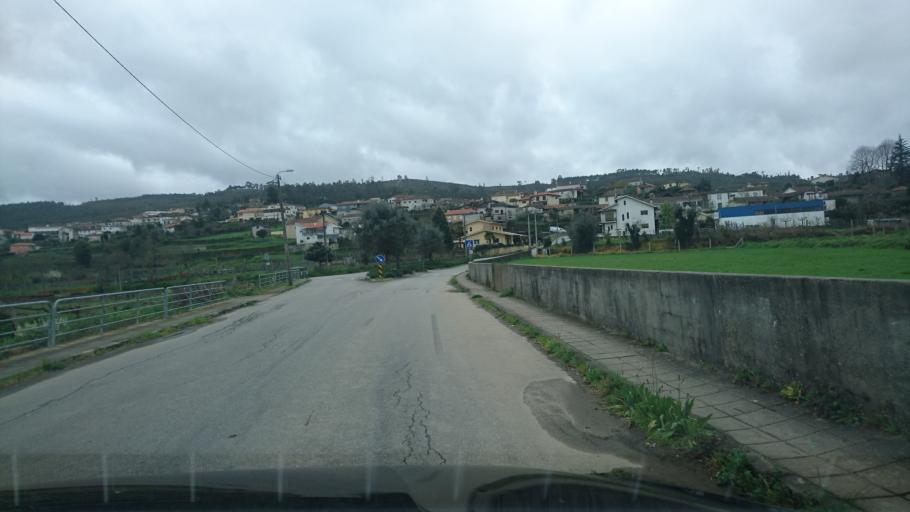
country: PT
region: Porto
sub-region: Paredes
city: Recarei
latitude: 41.1425
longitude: -8.3912
